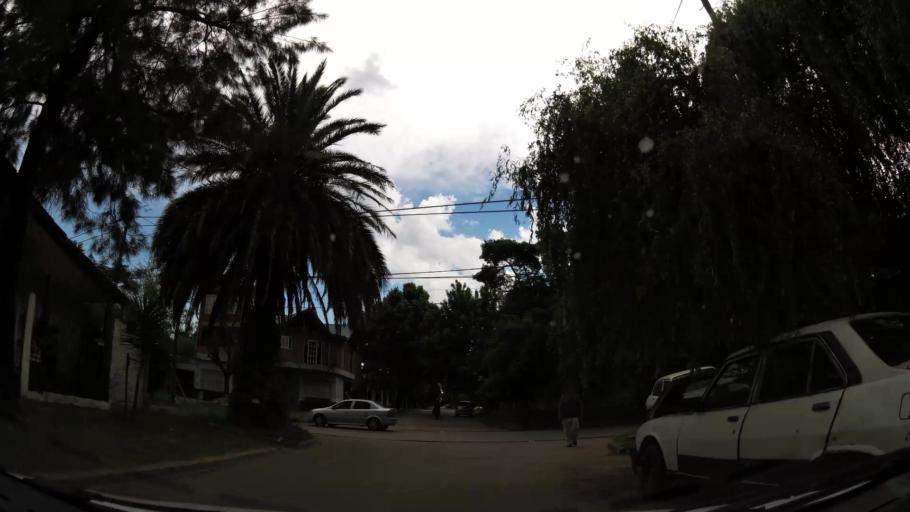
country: AR
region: Buenos Aires
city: Ituzaingo
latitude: -34.6315
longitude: -58.6913
